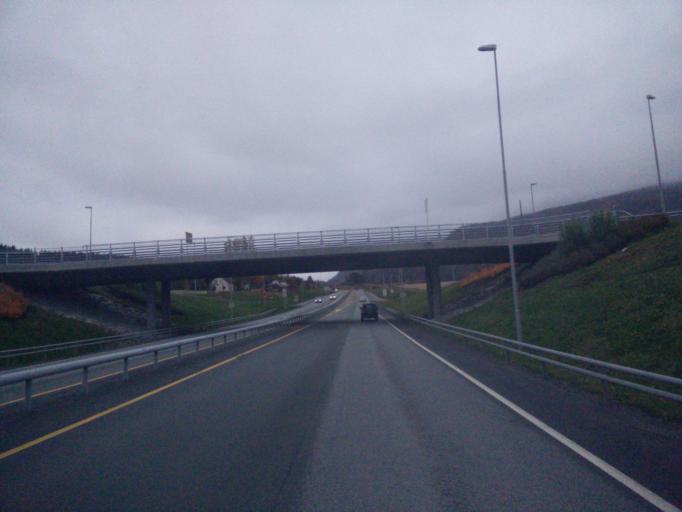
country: NO
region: Nord-Trondelag
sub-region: Stjordal
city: Stjordal
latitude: 63.4897
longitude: 10.8852
